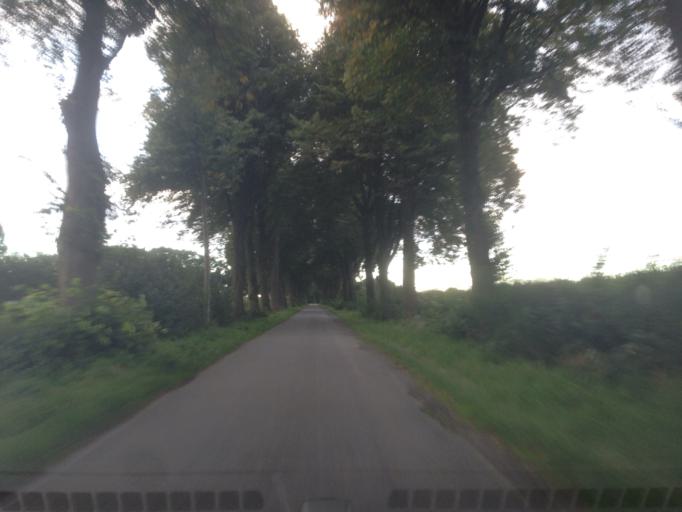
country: DE
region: North Rhine-Westphalia
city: Olfen
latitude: 51.7539
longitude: 7.3888
